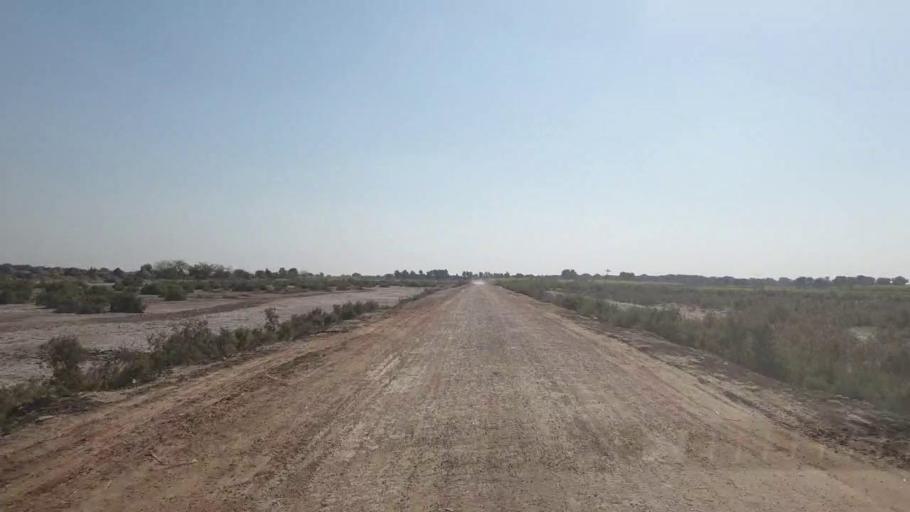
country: PK
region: Sindh
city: Chambar
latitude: 25.3224
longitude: 68.7398
